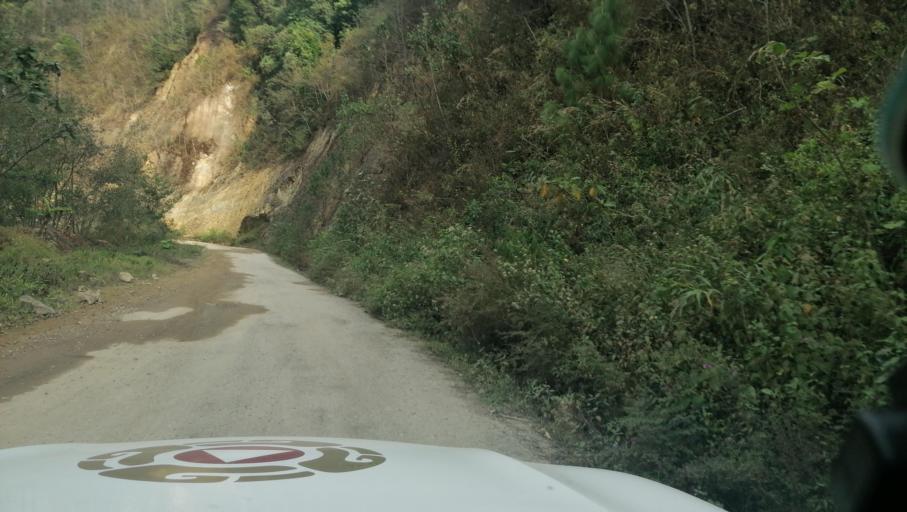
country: GT
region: San Marcos
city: Tacana
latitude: 15.2239
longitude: -92.1941
